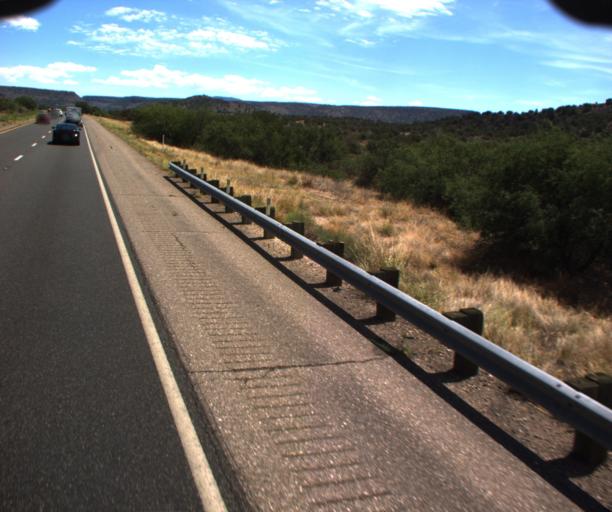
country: US
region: Arizona
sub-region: Yavapai County
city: Lake Montezuma
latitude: 34.6832
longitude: -111.7490
